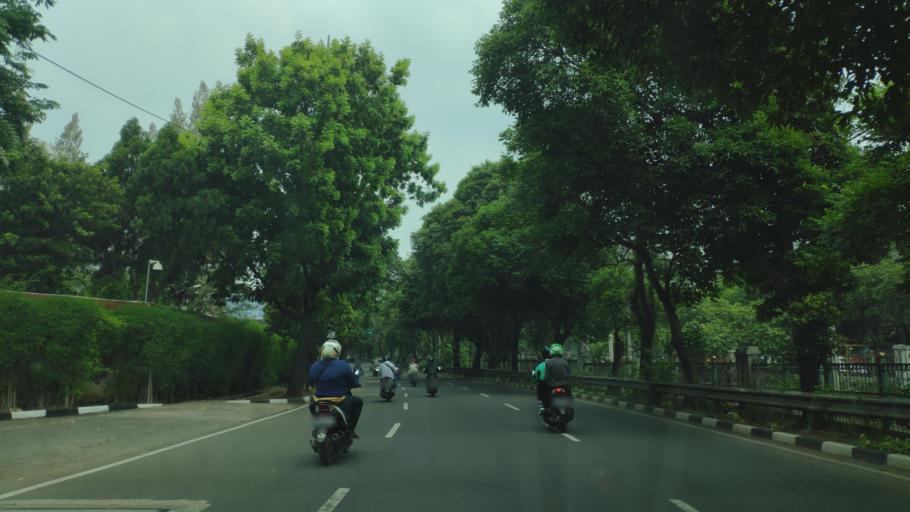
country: ID
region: Jakarta Raya
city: Jakarta
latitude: -6.2130
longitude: 106.7960
